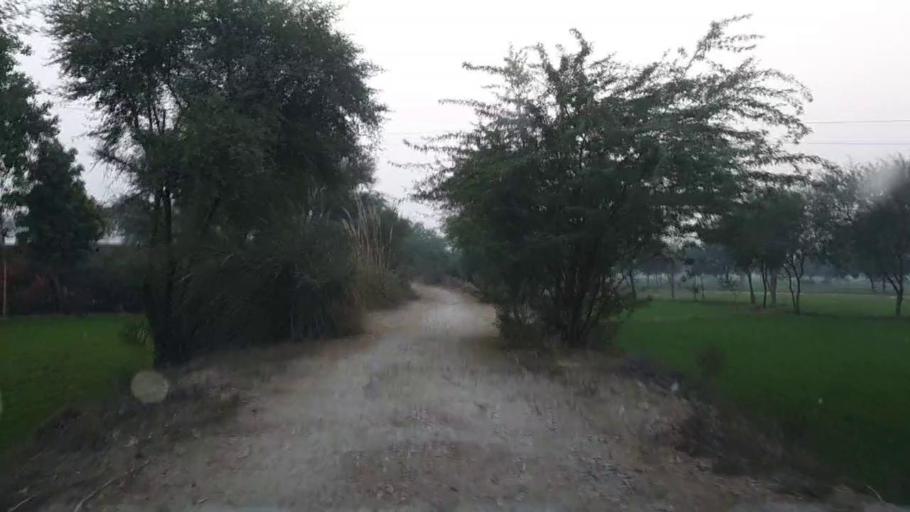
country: PK
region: Sindh
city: Kandiari
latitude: 26.9624
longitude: 68.4642
